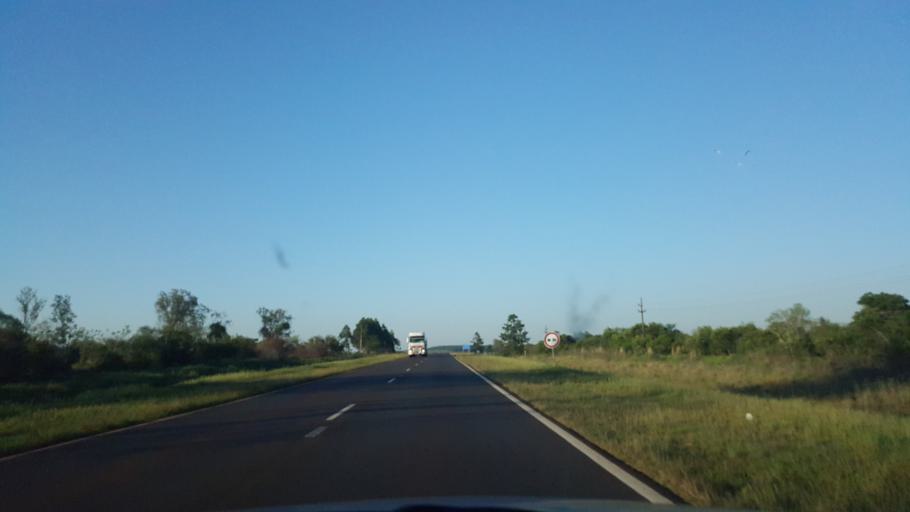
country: AR
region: Corrientes
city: Santo Tome
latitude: -28.4816
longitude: -56.1144
